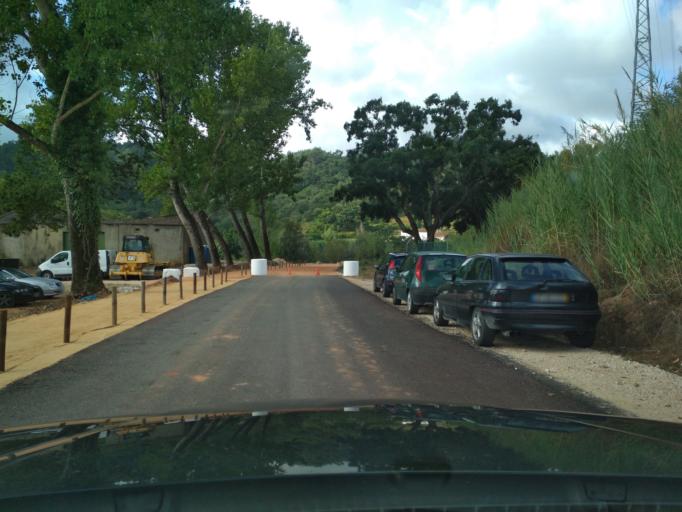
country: PT
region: Coimbra
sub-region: Coimbra
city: Coimbra
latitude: 40.1804
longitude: -8.4165
